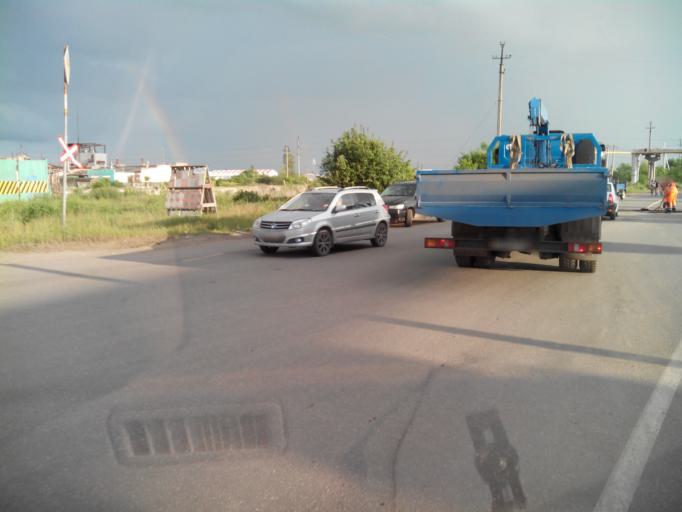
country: RU
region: Penza
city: Penza
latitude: 53.1312
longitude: 44.9978
